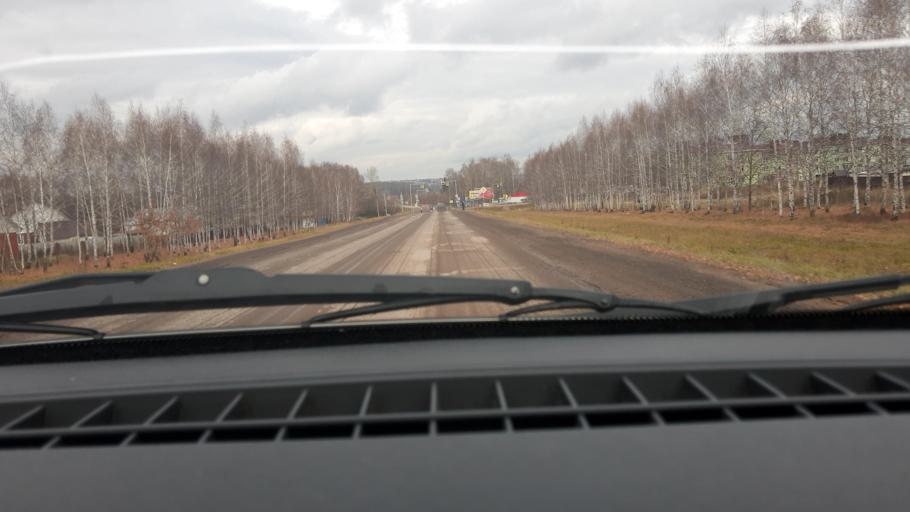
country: RU
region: Bashkortostan
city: Iglino
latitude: 54.8270
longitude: 56.4238
